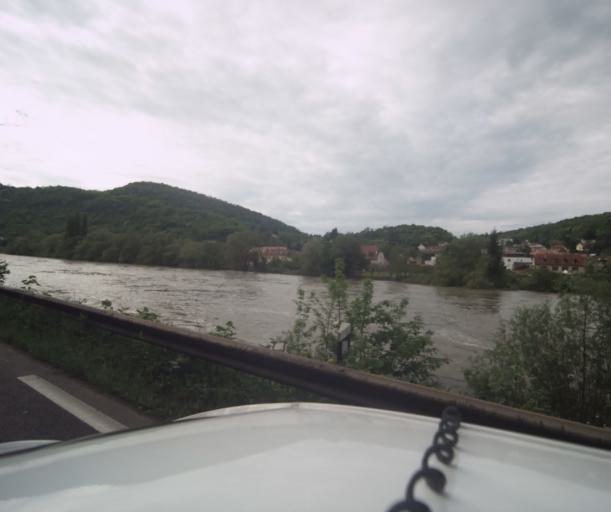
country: FR
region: Franche-Comte
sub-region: Departement du Doubs
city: Beure
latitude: 47.2168
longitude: 6.0152
